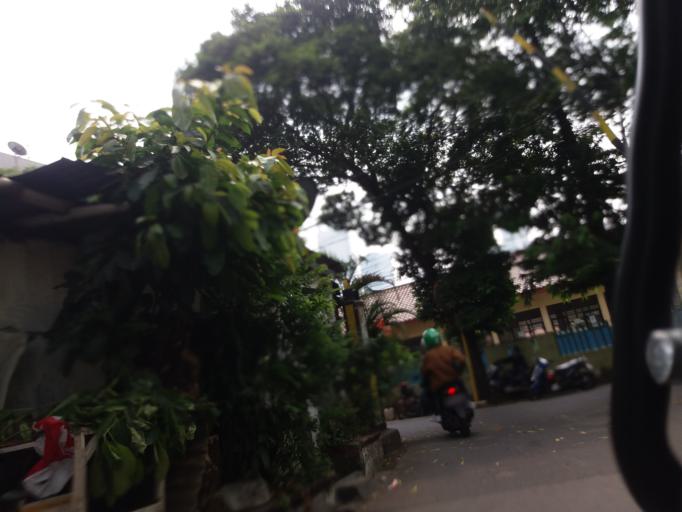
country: ID
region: Jakarta Raya
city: Jakarta
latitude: -6.2164
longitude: 106.8251
